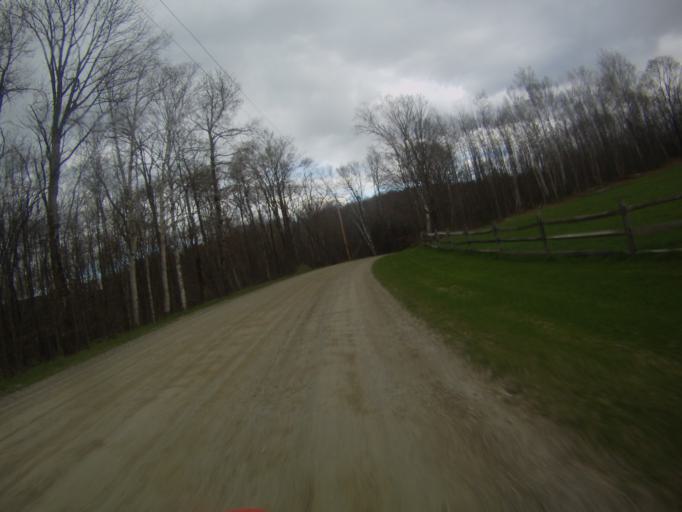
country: US
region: Vermont
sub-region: Addison County
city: Bristol
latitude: 44.0585
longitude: -73.0074
